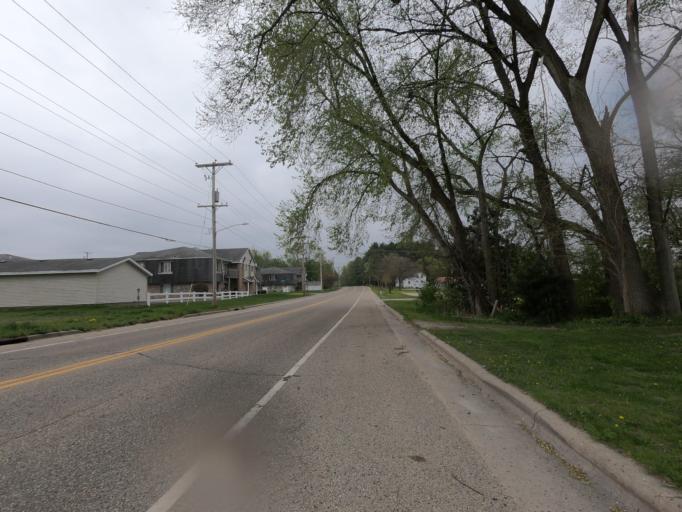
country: US
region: Wisconsin
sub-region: Jefferson County
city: Jefferson
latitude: 43.0225
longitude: -88.8102
